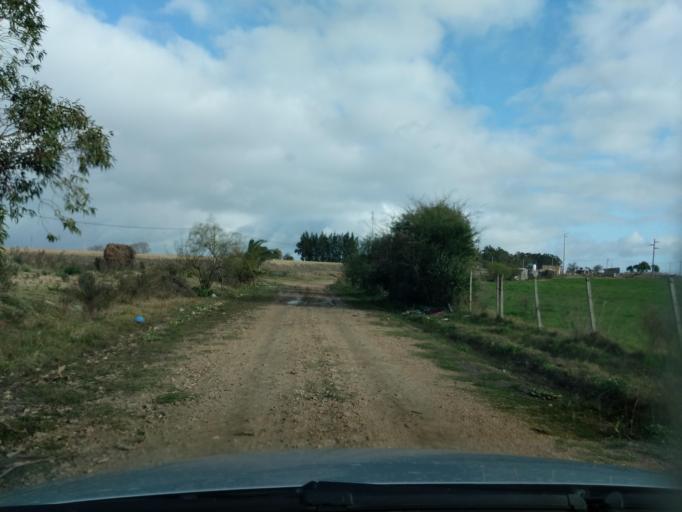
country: UY
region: Florida
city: Florida
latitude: -34.0759
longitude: -56.2308
